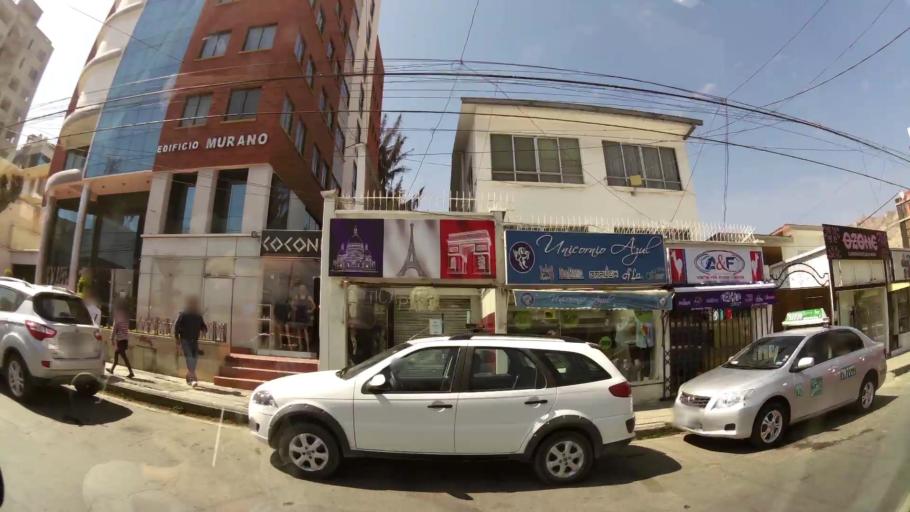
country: BO
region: La Paz
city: La Paz
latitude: -16.5411
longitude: -68.0768
